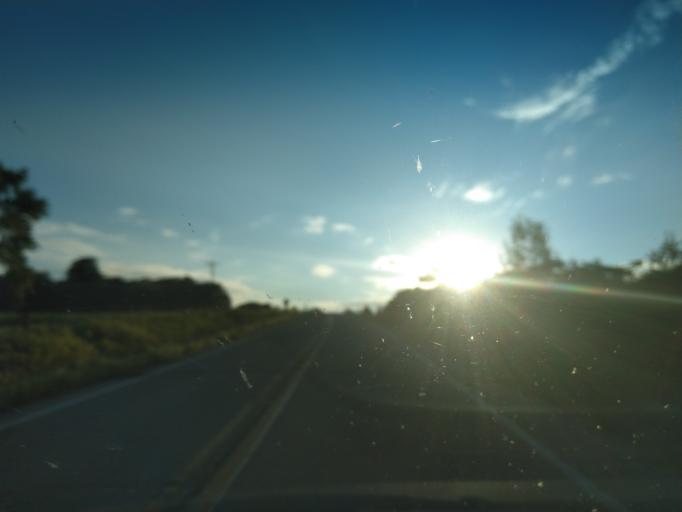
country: US
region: Iowa
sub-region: Jackson County
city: Maquoketa
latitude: 42.1644
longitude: -90.7316
